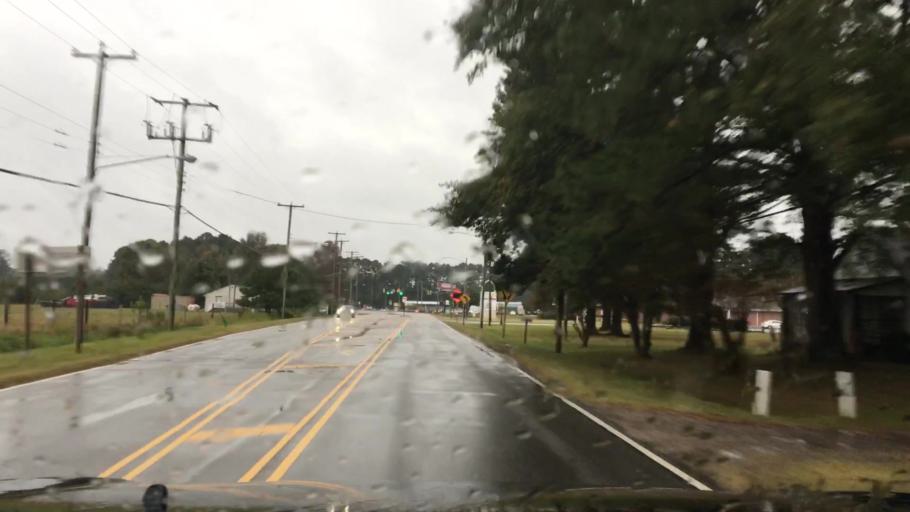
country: US
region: Virginia
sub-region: City of Chesapeake
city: Chesapeake
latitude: 36.6740
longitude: -76.2268
